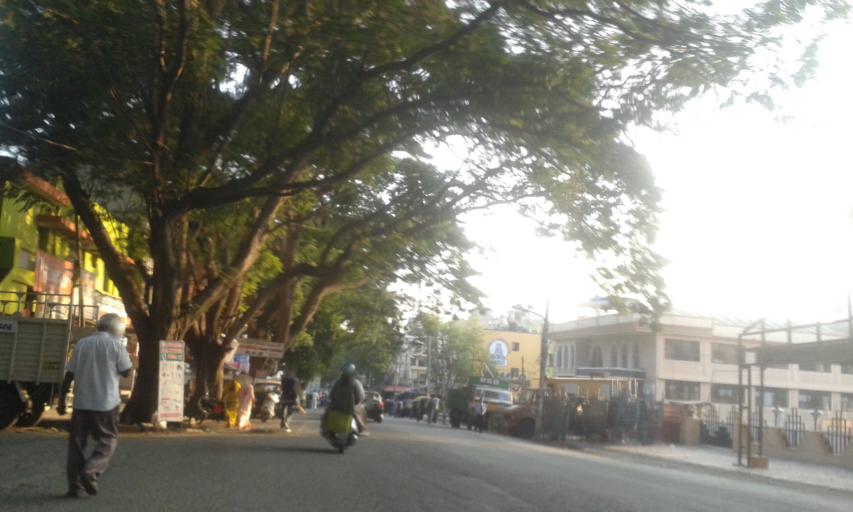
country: IN
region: Karnataka
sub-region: Bangalore Urban
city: Bangalore
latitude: 12.9199
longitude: 77.5896
